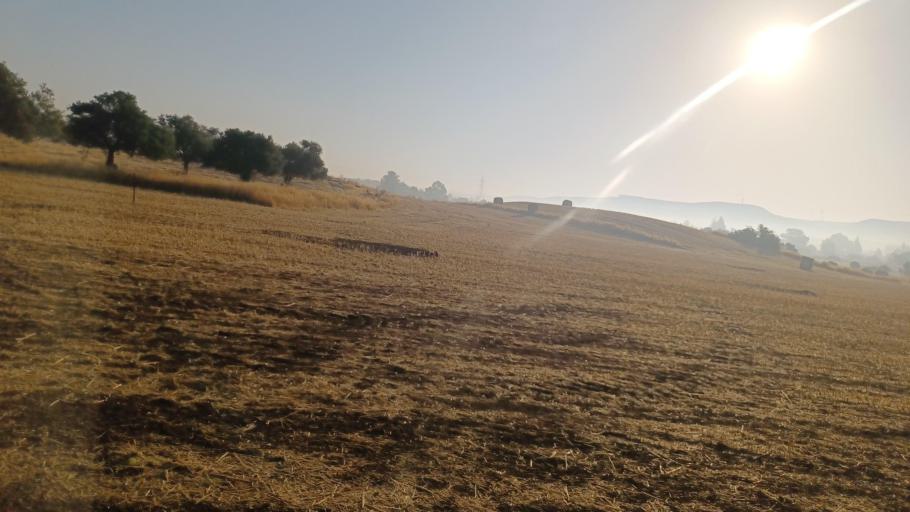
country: CY
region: Larnaka
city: Mosfiloti
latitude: 34.9758
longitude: 33.4364
